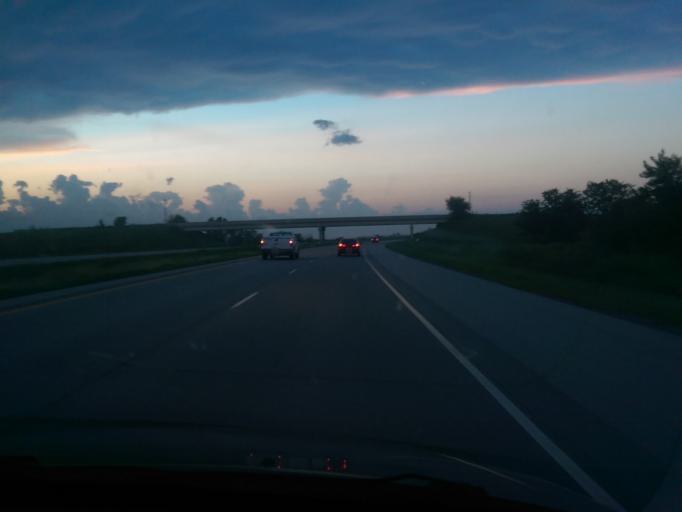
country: US
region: Nebraska
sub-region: Otoe County
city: Nebraska City
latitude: 40.7567
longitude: -95.8174
